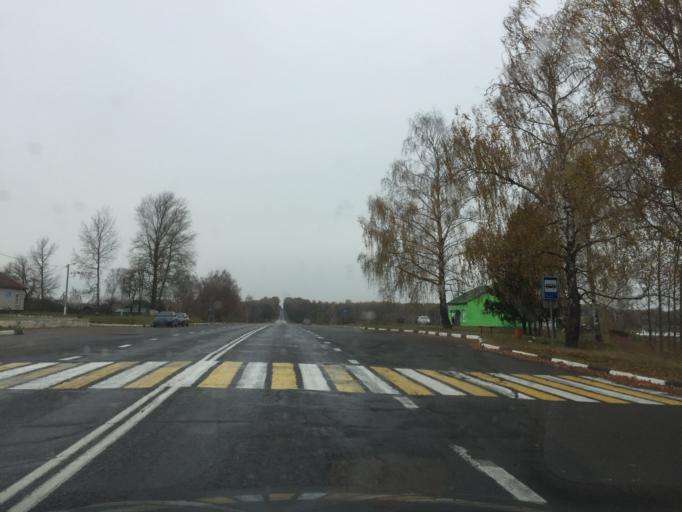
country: BY
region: Gomel
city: Karma
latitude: 53.3420
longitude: 30.8049
